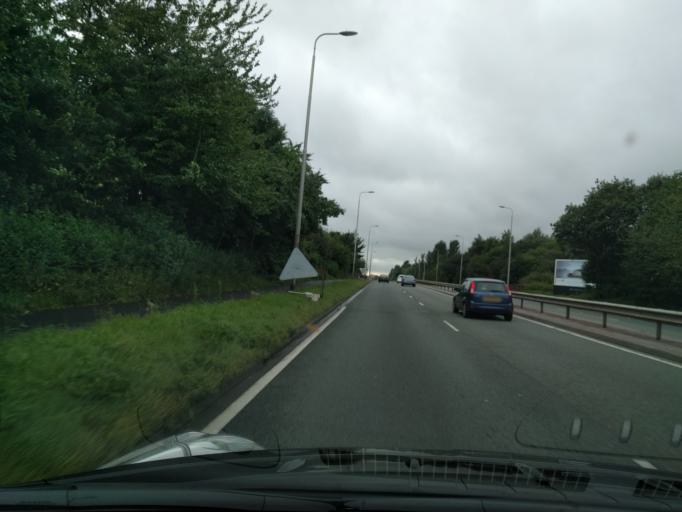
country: GB
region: England
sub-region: Borough of Wigan
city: Ashton in Makerfield
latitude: 53.4725
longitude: -2.6581
